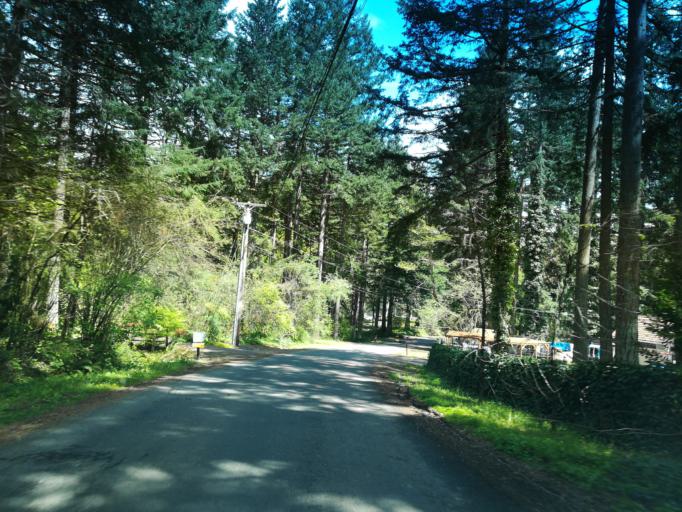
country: US
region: Oregon
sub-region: Clackamas County
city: Damascus
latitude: 45.4427
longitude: -122.4611
